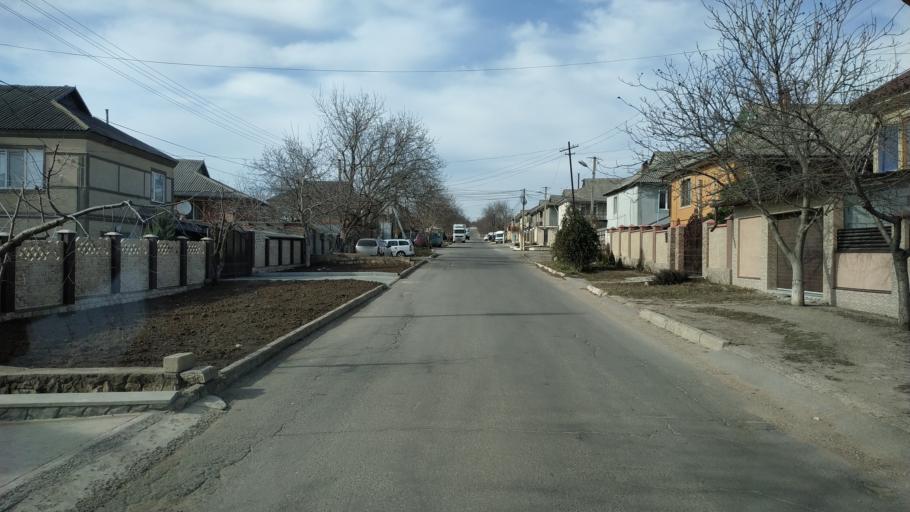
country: MD
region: Chisinau
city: Vatra
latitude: 47.0764
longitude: 28.6910
